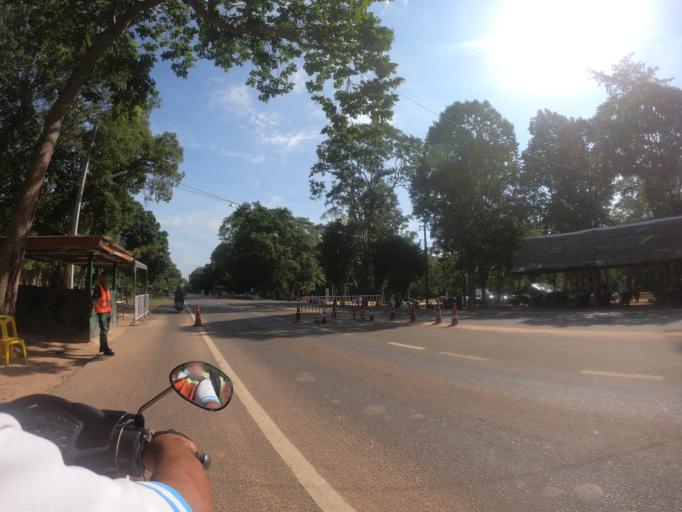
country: TH
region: Surin
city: Kap Choeng
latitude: 14.4403
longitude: 103.7007
